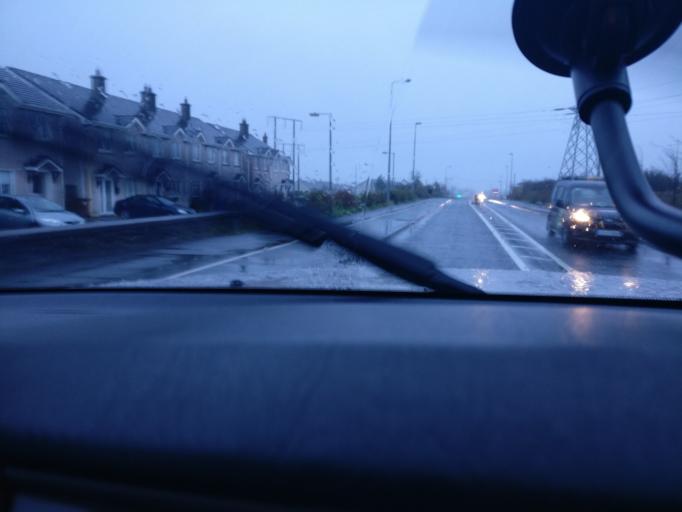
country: IE
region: Connaught
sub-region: County Galway
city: Gaillimh
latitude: 53.2895
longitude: -8.9871
